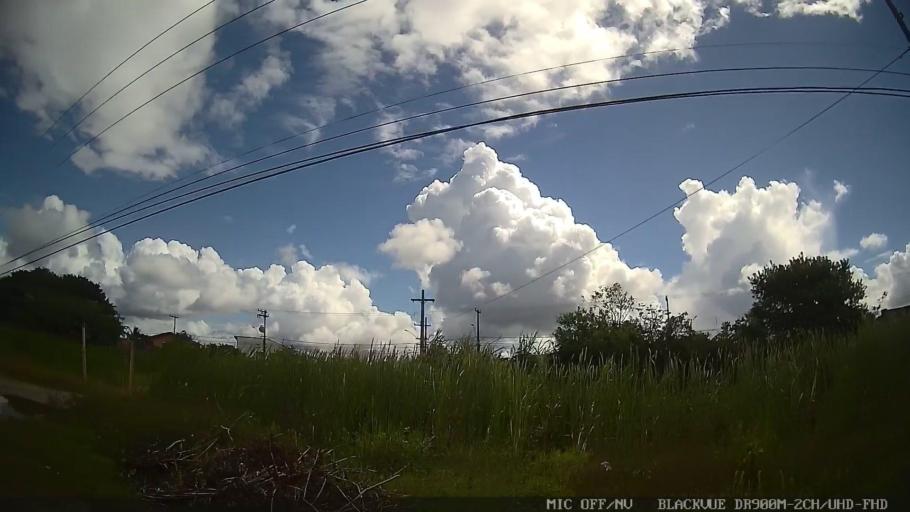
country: BR
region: Sao Paulo
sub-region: Itanhaem
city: Itanhaem
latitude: -24.2230
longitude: -46.8676
